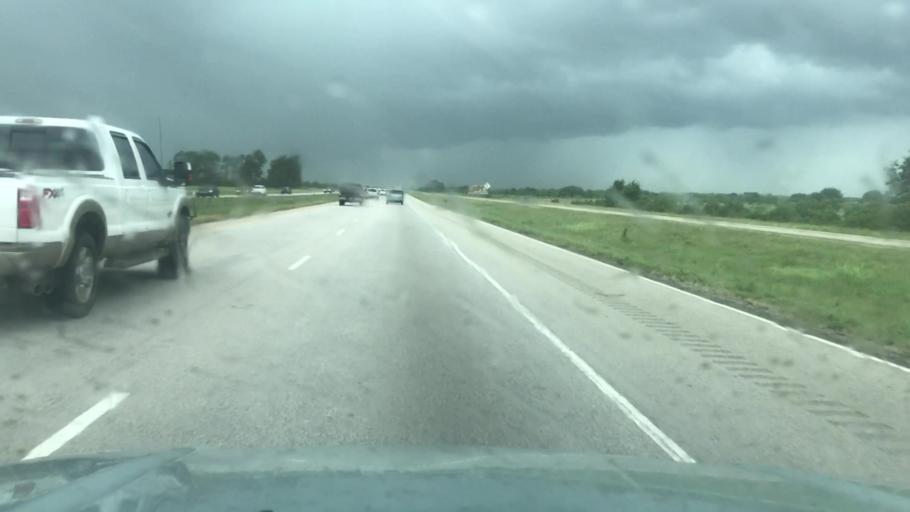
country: US
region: Texas
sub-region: Austin County
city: Sealy
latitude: 29.7478
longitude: -96.3004
